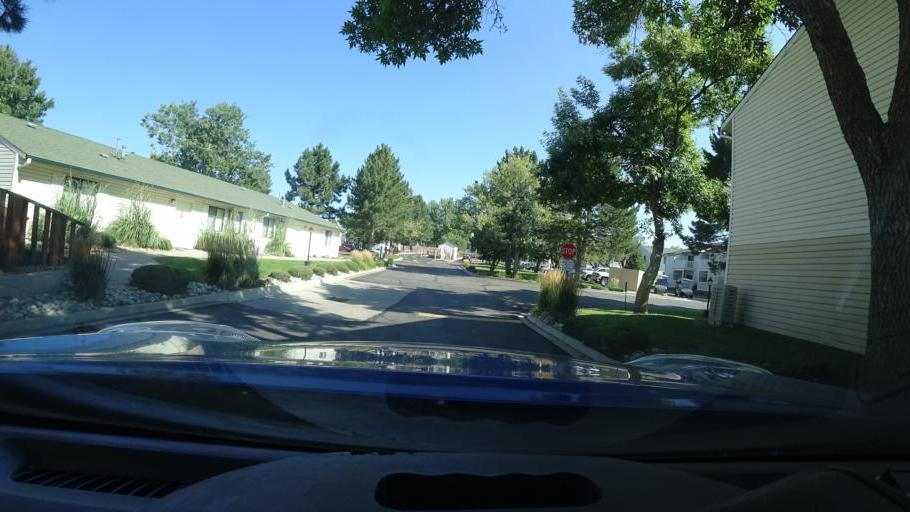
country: US
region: Colorado
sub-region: Adams County
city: Aurora
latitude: 39.7238
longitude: -104.8148
